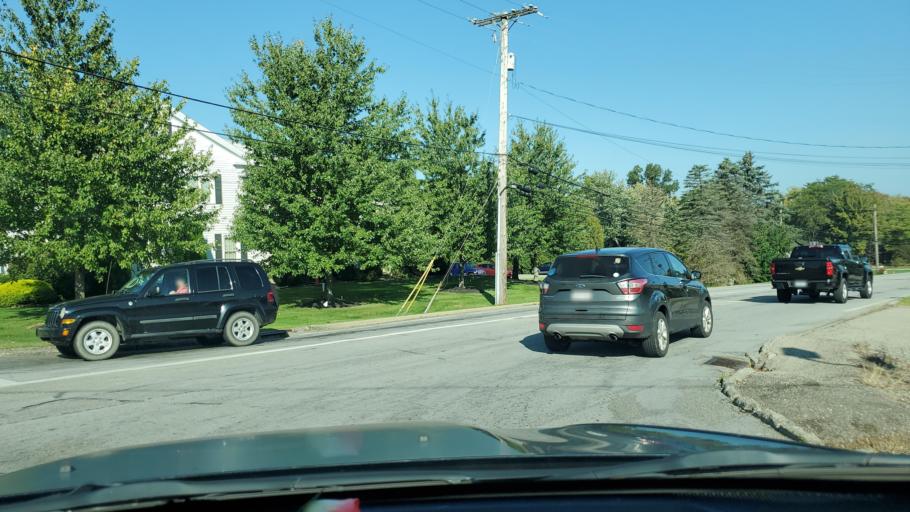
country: US
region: Ohio
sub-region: Trumbull County
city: Brookfield Center
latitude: 41.2342
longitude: -80.5680
